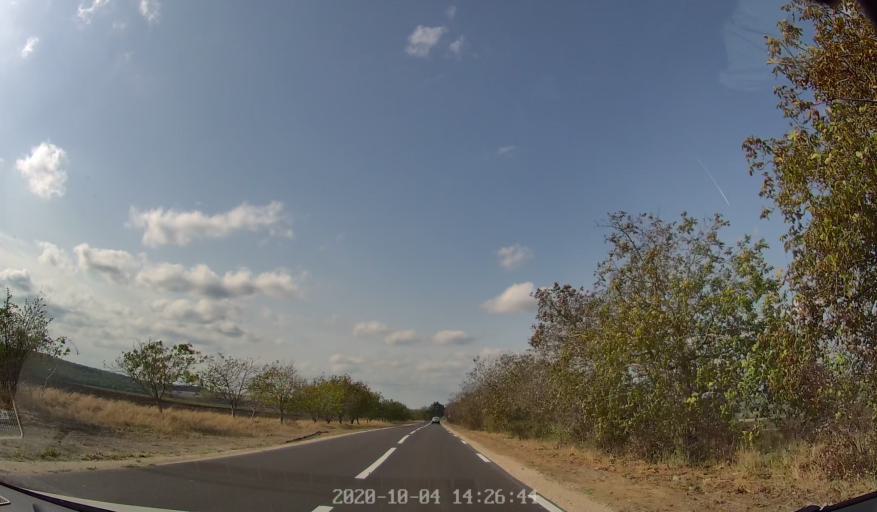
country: MD
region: Rezina
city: Saharna
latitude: 47.6294
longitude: 28.8794
